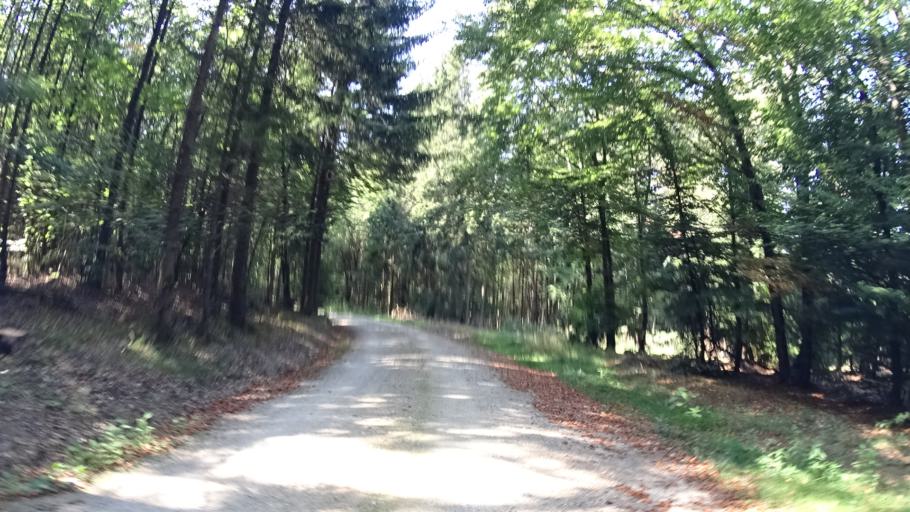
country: DE
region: Bavaria
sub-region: Regierungsbezirk Mittelfranken
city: Greding
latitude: 48.9750
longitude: 11.3482
